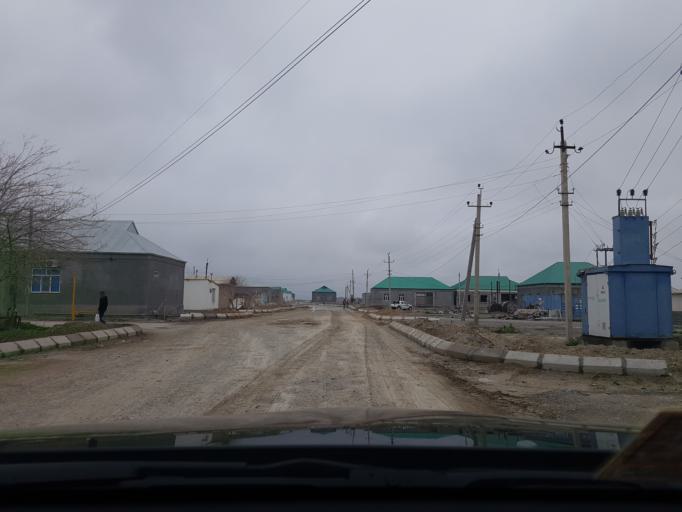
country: TM
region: Ahal
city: Abadan
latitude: 38.1461
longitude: 57.9490
